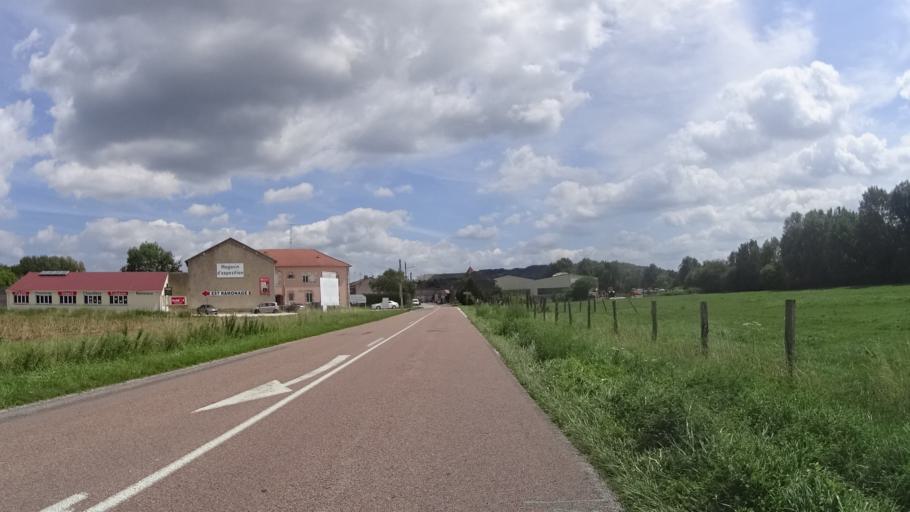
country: FR
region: Lorraine
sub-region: Departement de la Meuse
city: Euville
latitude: 48.7380
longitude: 5.6579
